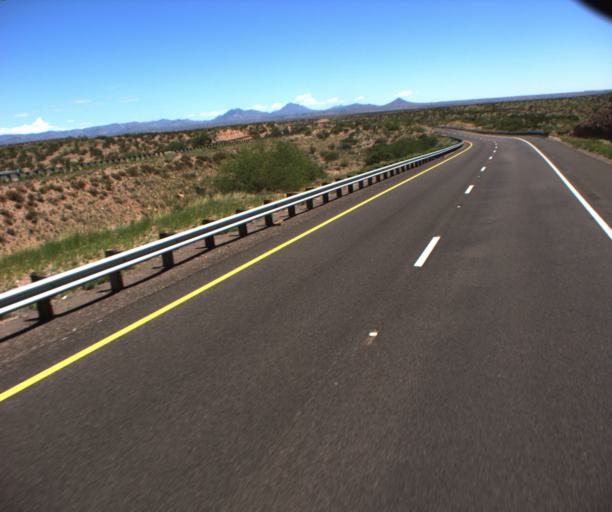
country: US
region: Arizona
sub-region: Greenlee County
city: Clifton
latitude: 32.9759
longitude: -109.2481
